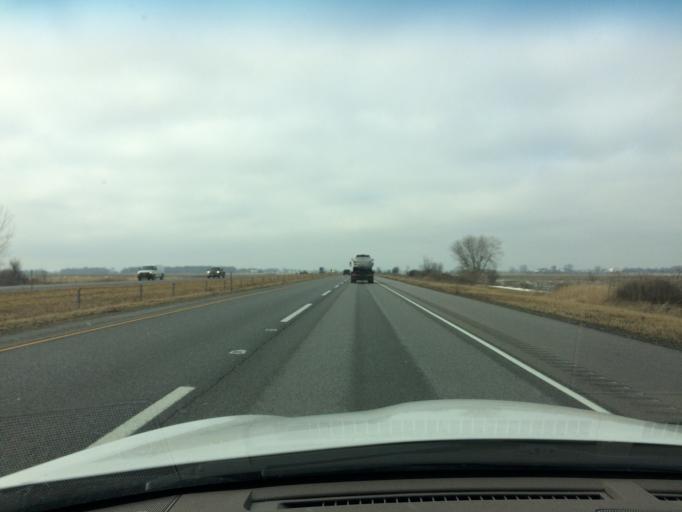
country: US
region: Illinois
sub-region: Kane County
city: Elburn
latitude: 41.8582
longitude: -88.5334
